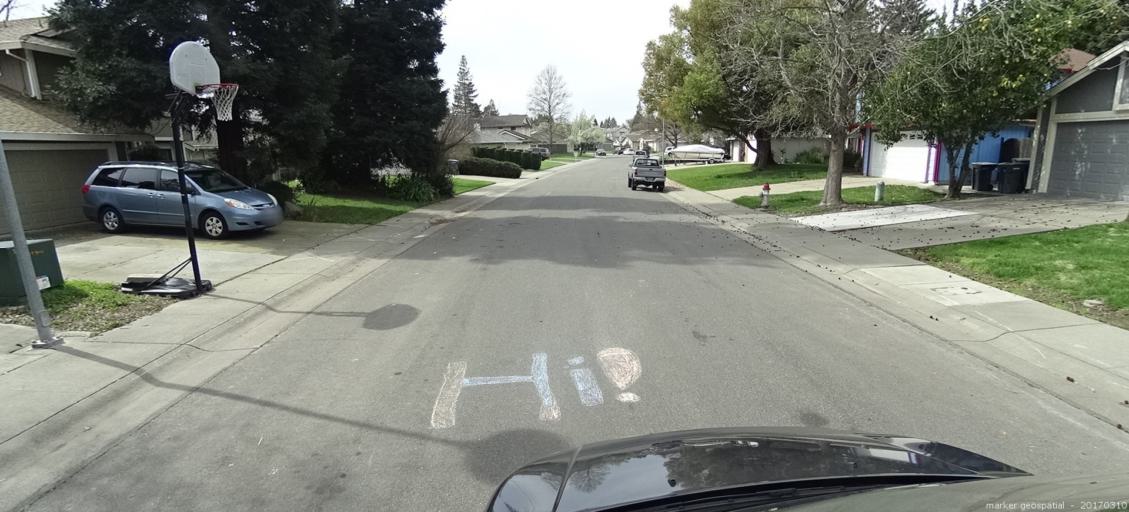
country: US
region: California
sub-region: Sacramento County
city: Parkway
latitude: 38.4807
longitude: -121.5365
